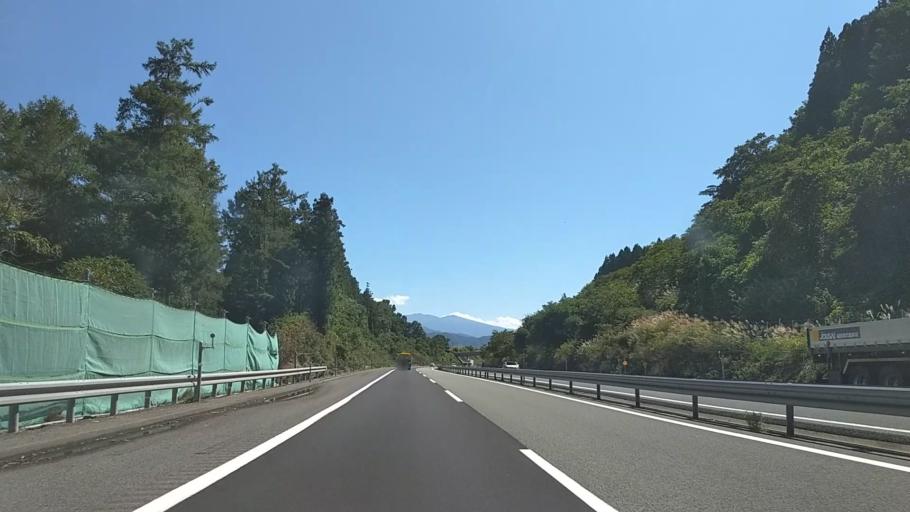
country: JP
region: Nagano
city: Nakano
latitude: 36.7784
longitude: 138.3177
